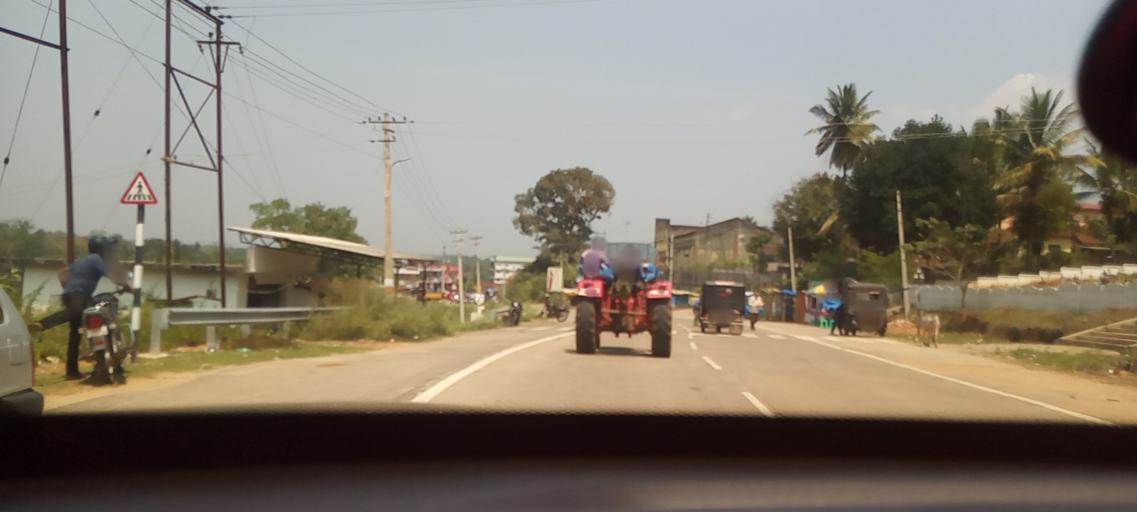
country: IN
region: Karnataka
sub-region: Chikmagalur
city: Koppa
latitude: 13.3481
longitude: 75.4624
